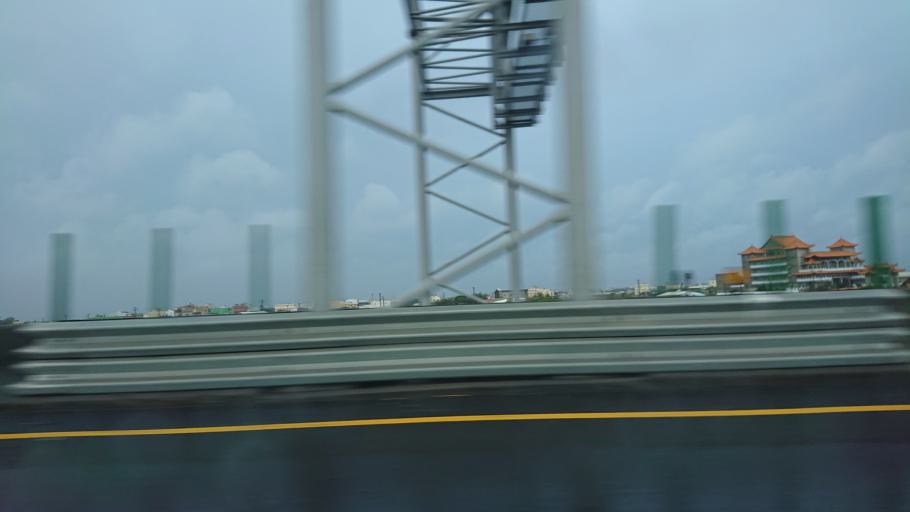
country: TW
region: Taiwan
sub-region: Changhua
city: Chang-hua
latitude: 24.1497
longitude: 120.4530
